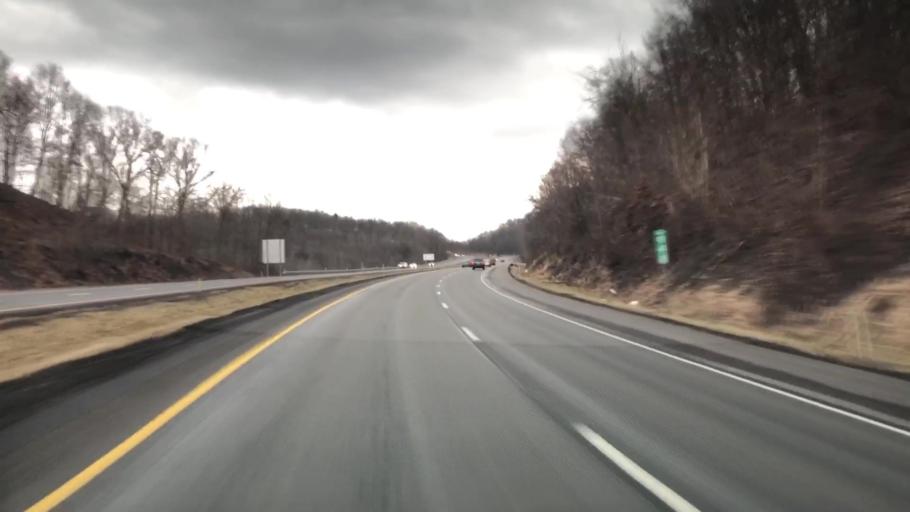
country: US
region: Pennsylvania
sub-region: Butler County
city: Prospect
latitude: 40.9052
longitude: -80.1228
